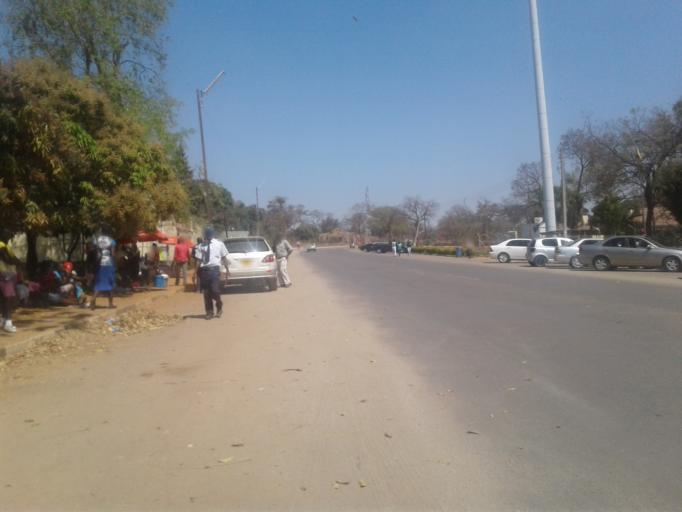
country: ZW
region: Mashonaland West
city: Chinhoyi
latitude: -17.3609
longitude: 30.1940
